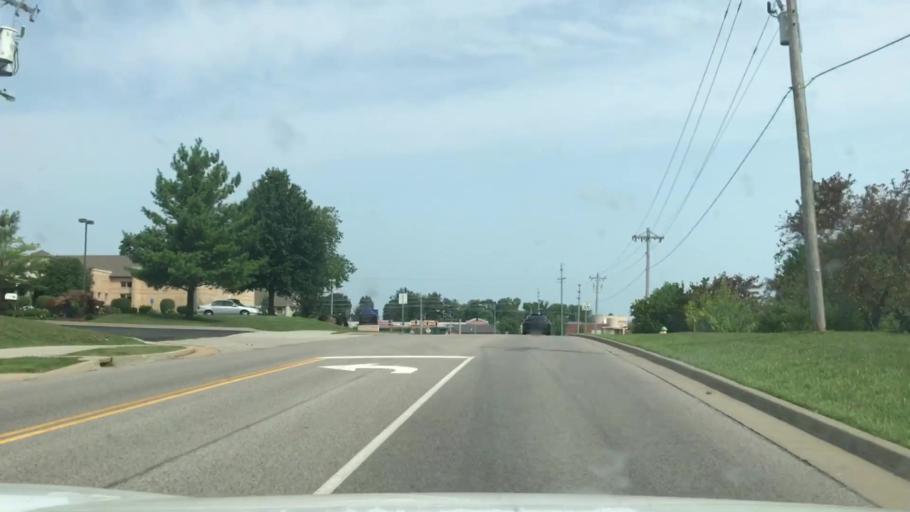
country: US
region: Missouri
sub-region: Saint Charles County
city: Cottleville
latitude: 38.7259
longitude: -90.6435
